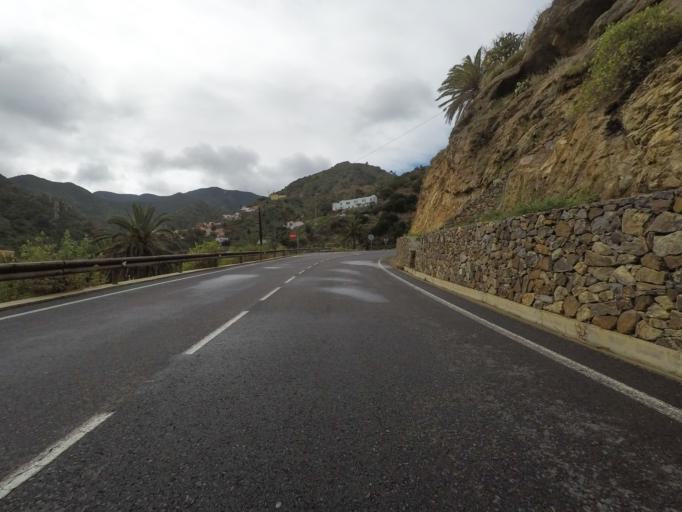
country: ES
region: Canary Islands
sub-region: Provincia de Santa Cruz de Tenerife
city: Vallehermosa
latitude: 28.1717
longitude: -17.2733
